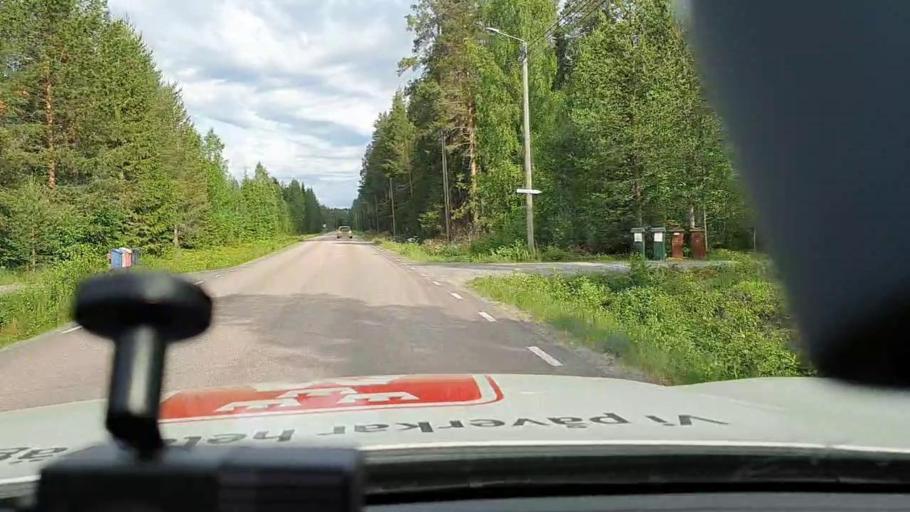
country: SE
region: Norrbotten
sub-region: Bodens Kommun
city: Saevast
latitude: 65.7258
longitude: 21.7481
